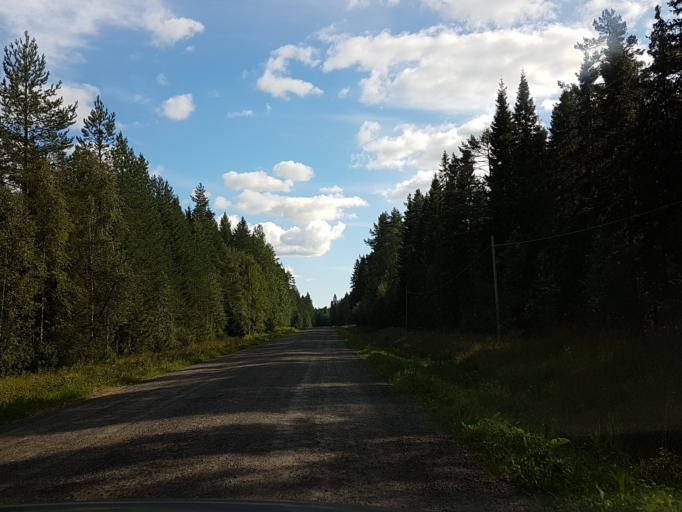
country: SE
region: Vaesterbotten
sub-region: Robertsfors Kommun
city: Robertsfors
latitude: 64.1756
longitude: 20.6457
